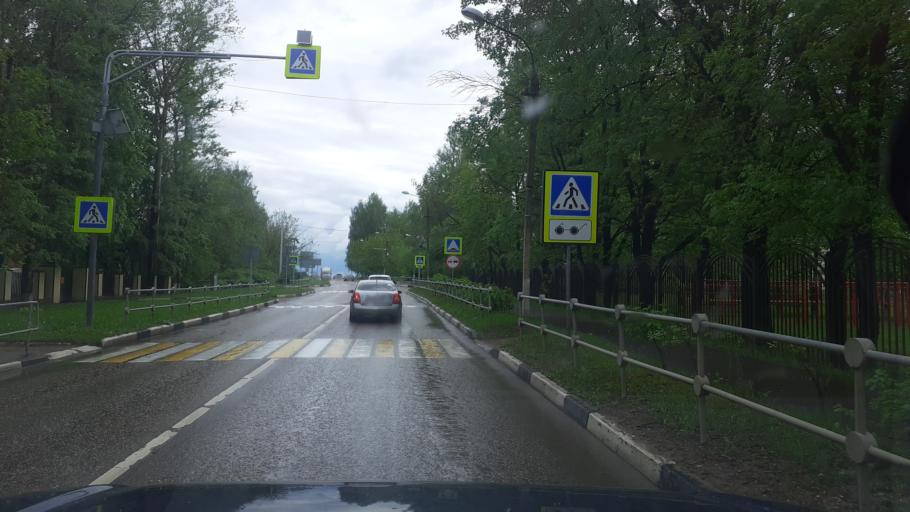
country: RU
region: Moskovskaya
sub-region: Volokolamskiy Rayon
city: Volokolamsk
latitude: 56.0274
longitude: 35.9626
